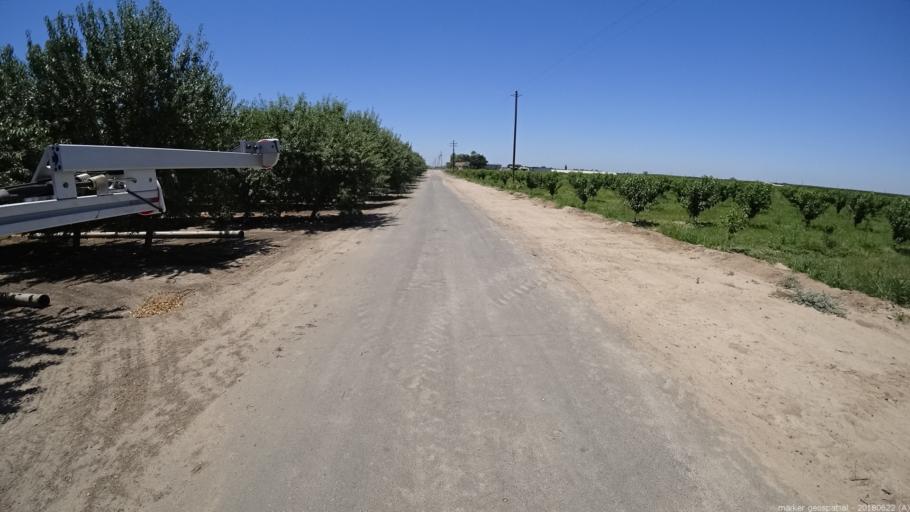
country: US
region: California
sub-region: Madera County
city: Parksdale
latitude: 36.9021
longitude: -119.9928
